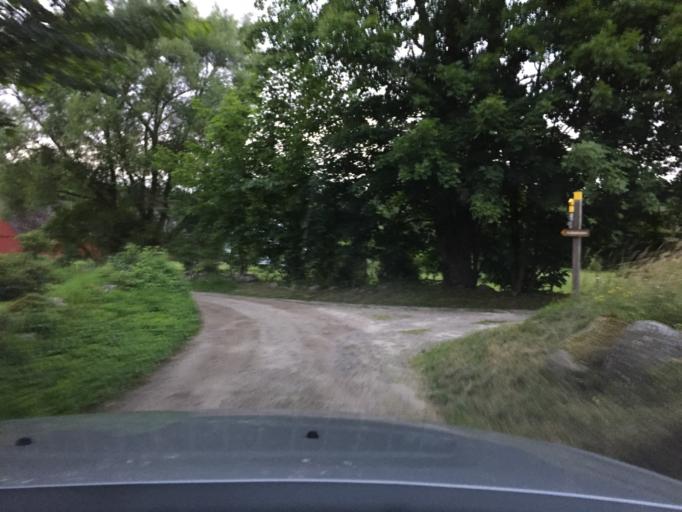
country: SE
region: Skane
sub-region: Kristianstads Kommun
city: Degeberga
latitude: 55.7259
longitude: 14.1277
